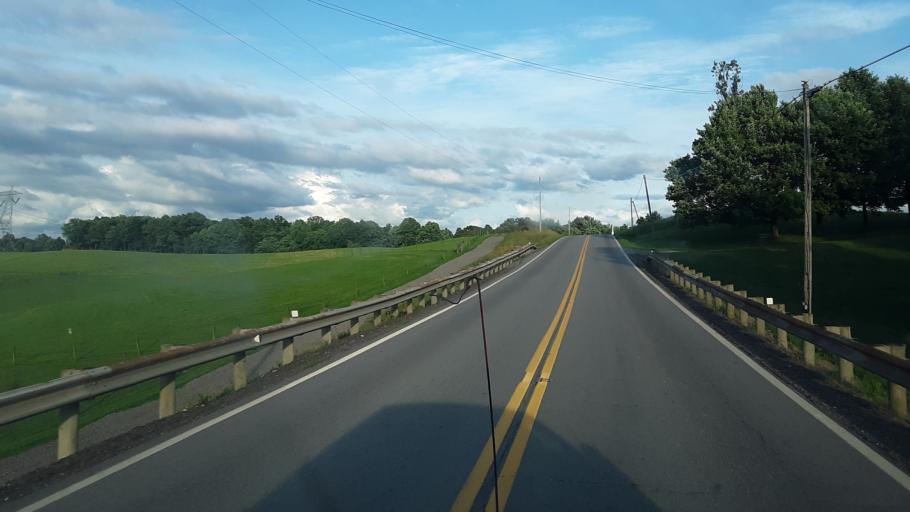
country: US
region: Ohio
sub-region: Carroll County
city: Carrollton
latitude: 40.4532
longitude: -80.9892
